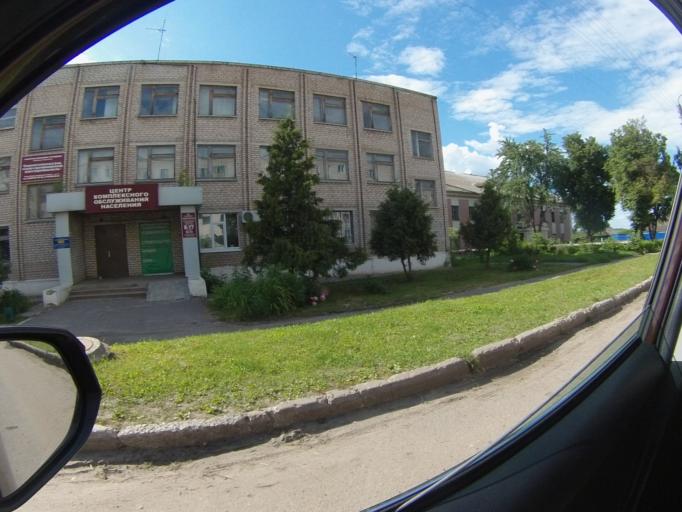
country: RU
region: Orjol
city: Mtsensk
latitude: 53.2823
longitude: 36.5705
